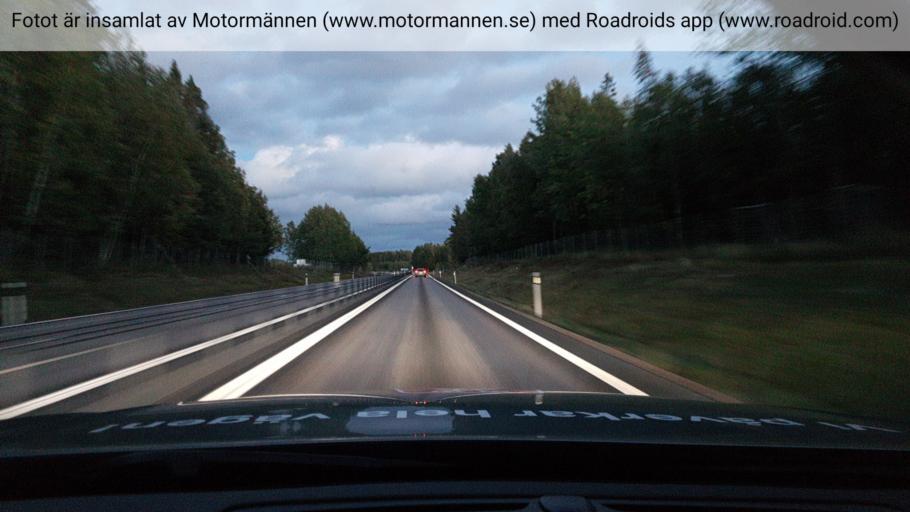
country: SE
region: Vaermland
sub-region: Kristinehamns Kommun
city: Kristinehamn
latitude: 59.3845
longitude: 13.8757
